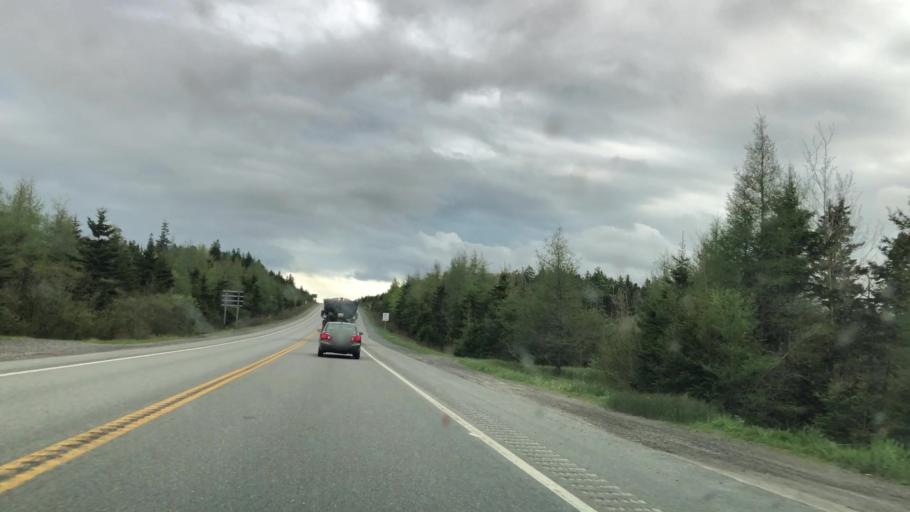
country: CA
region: Nova Scotia
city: Cole Harbour
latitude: 44.7797
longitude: -63.1777
